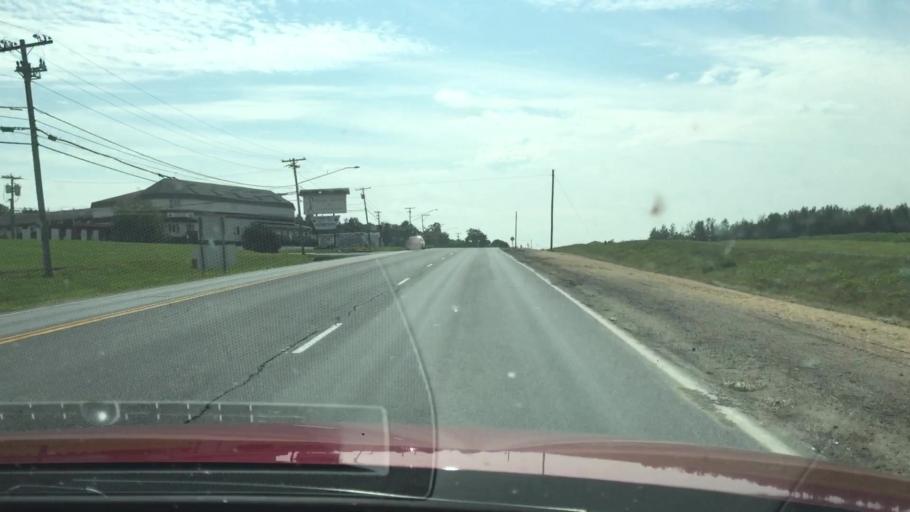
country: US
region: Maine
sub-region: Aroostook County
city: Presque Isle
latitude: 46.6687
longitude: -68.0127
